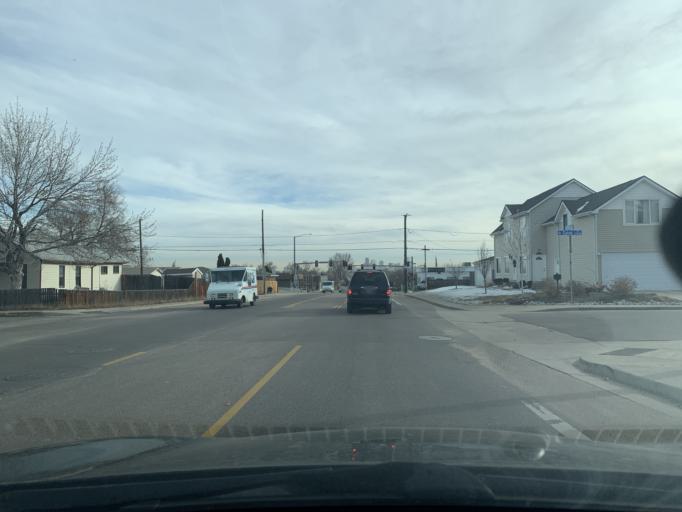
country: US
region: Colorado
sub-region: Jefferson County
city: Edgewater
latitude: 39.7476
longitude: -105.0594
